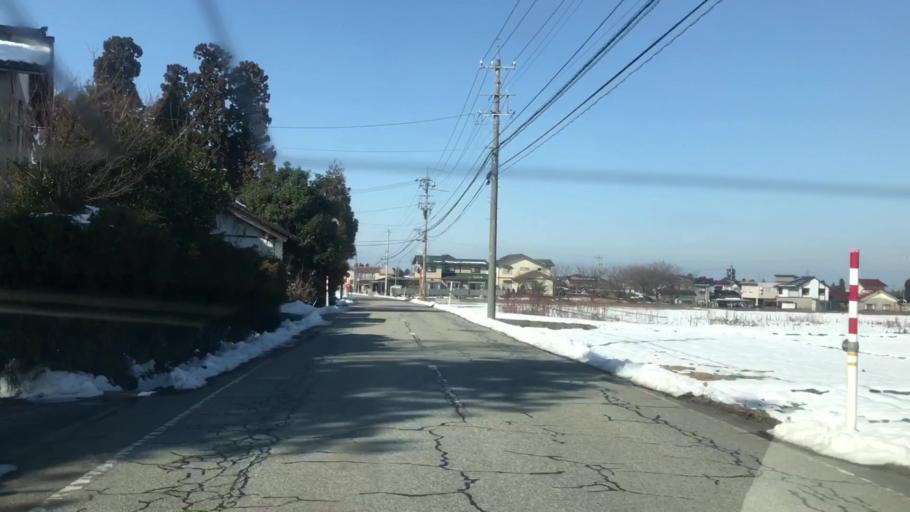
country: JP
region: Toyama
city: Toyama-shi
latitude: 36.6224
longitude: 137.2820
